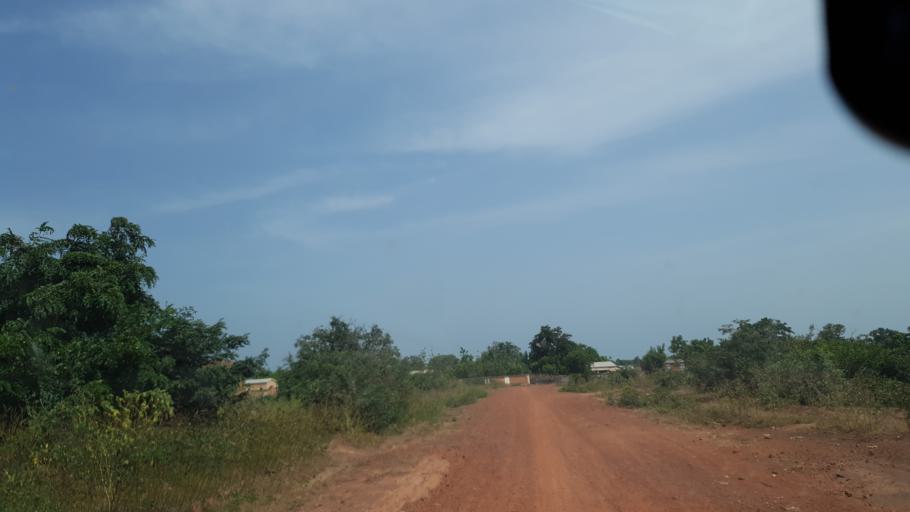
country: ML
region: Koulikoro
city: Dioila
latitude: 12.4767
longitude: -6.1847
